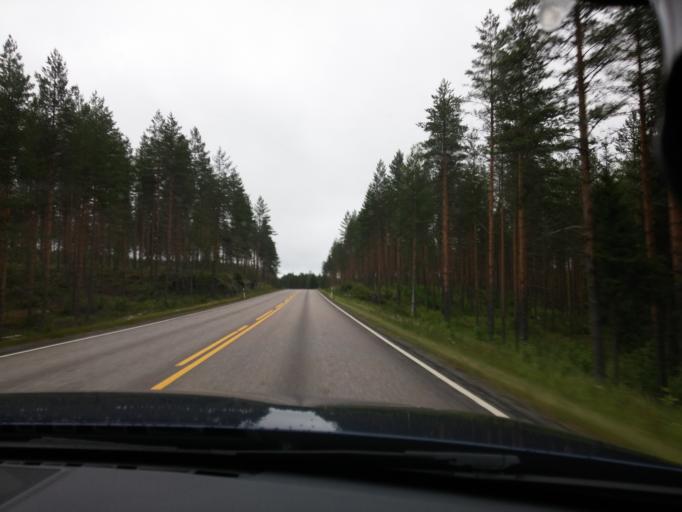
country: FI
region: Pirkanmaa
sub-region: Ylae-Pirkanmaa
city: Vilppula
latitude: 61.9201
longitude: 24.5367
